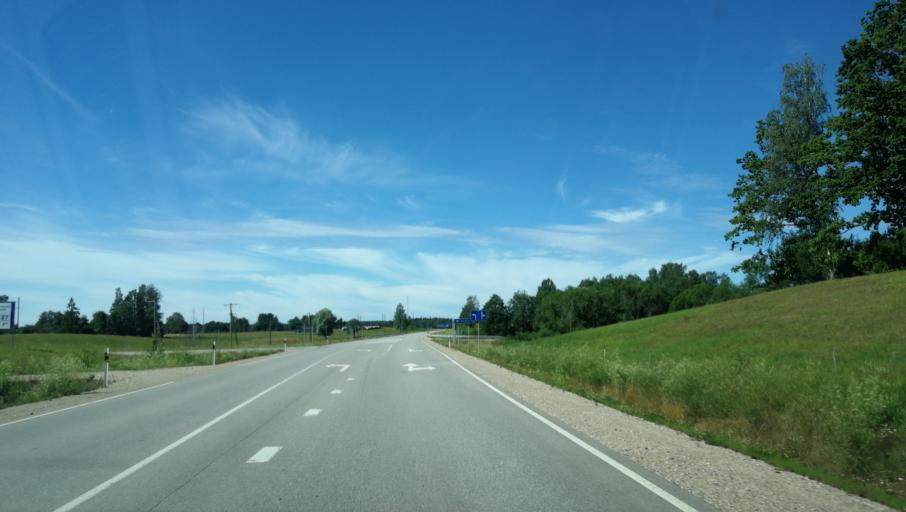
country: LV
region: Gulbenes Rajons
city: Gulbene
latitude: 57.0844
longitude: 26.6121
